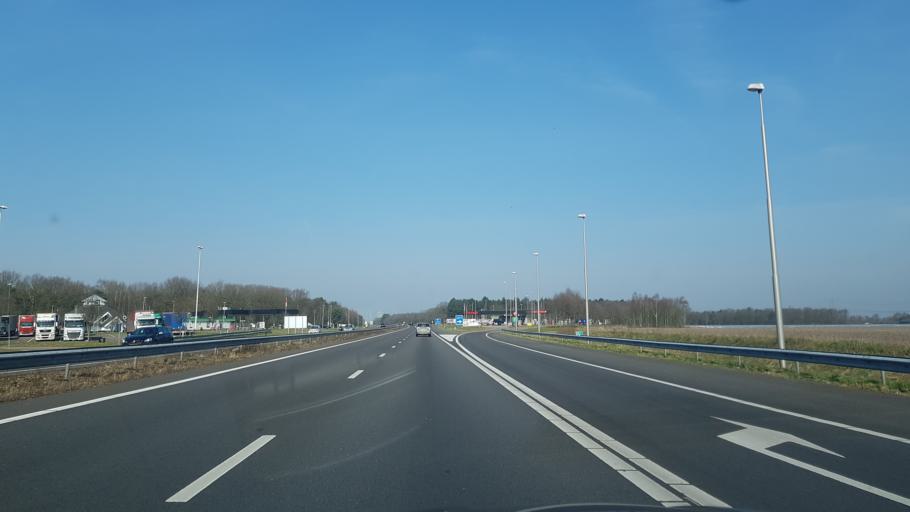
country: NL
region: Limburg
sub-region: Gemeente Venray
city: Venray
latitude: 51.5035
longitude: 6.0244
